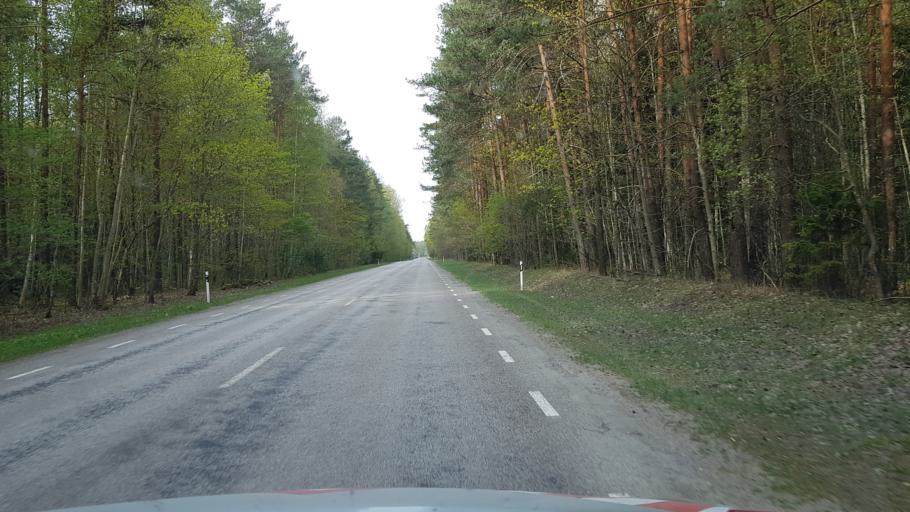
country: EE
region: Paernumaa
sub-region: Audru vald
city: Audru
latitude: 58.4110
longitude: 24.3437
